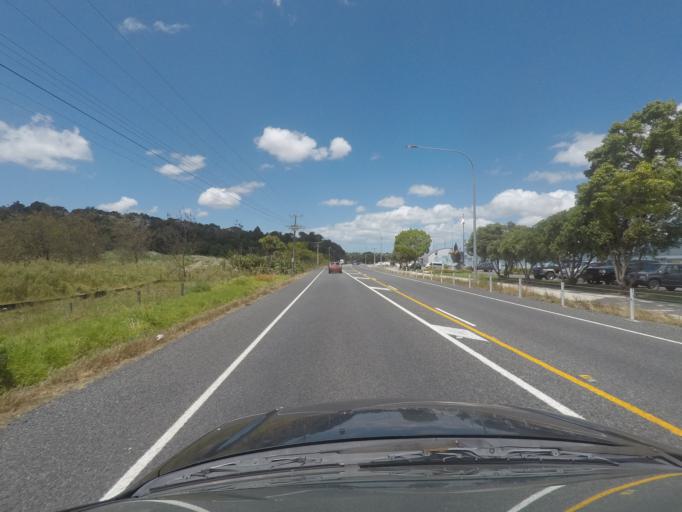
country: NZ
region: Northland
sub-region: Whangarei
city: Whangarei
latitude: -35.7335
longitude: 174.3481
